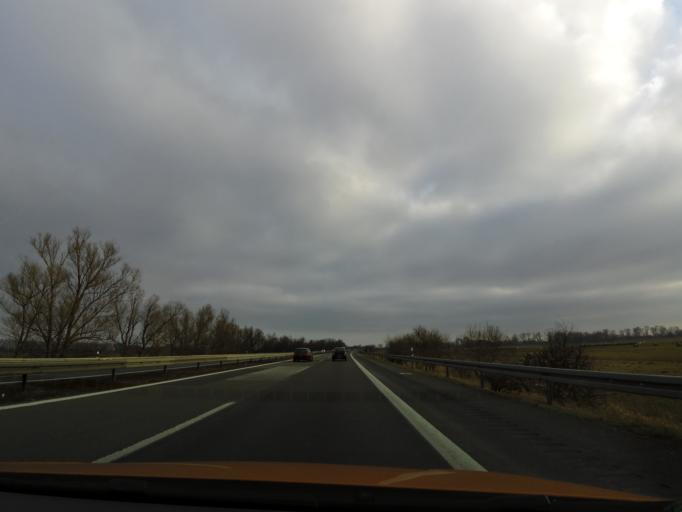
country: DE
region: Brandenburg
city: Fehrbellin
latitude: 52.8318
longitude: 12.7925
